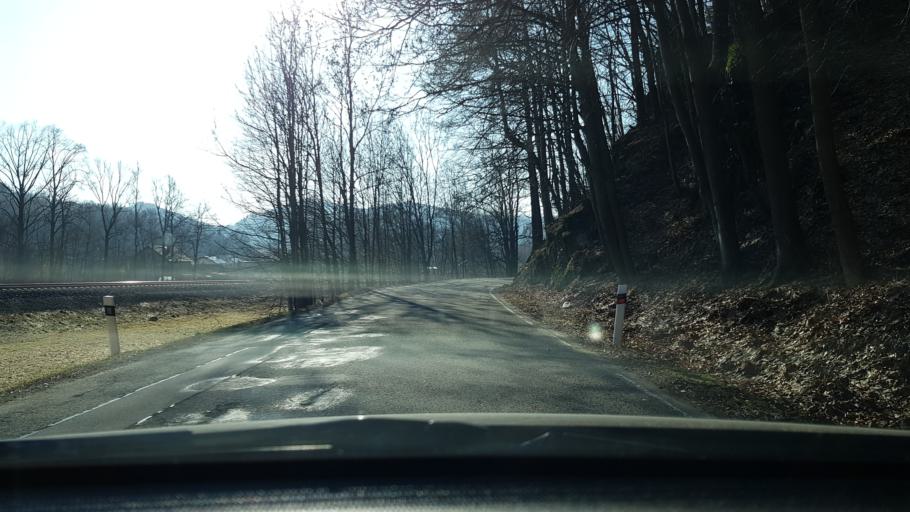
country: CZ
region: Olomoucky
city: Dolni Bohdikov
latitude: 50.0174
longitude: 16.8979
